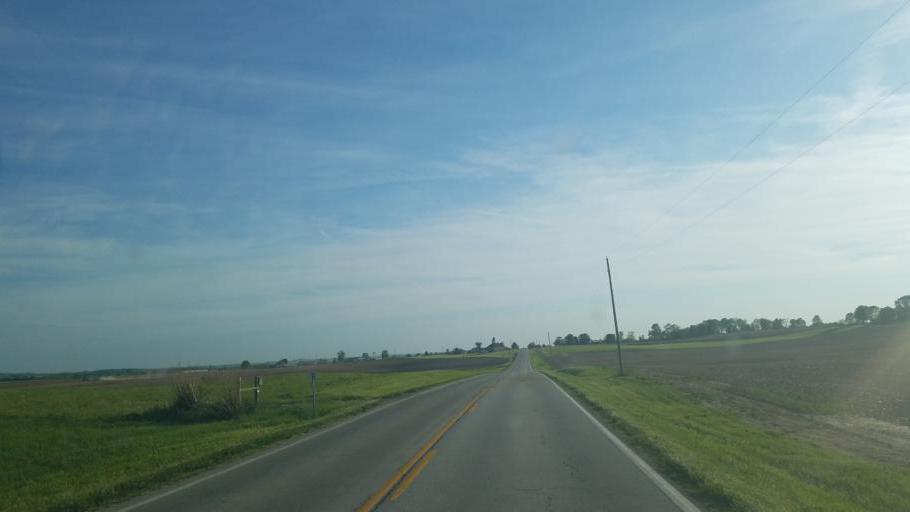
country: US
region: Ohio
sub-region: Highland County
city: Greenfield
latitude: 39.3719
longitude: -83.3547
